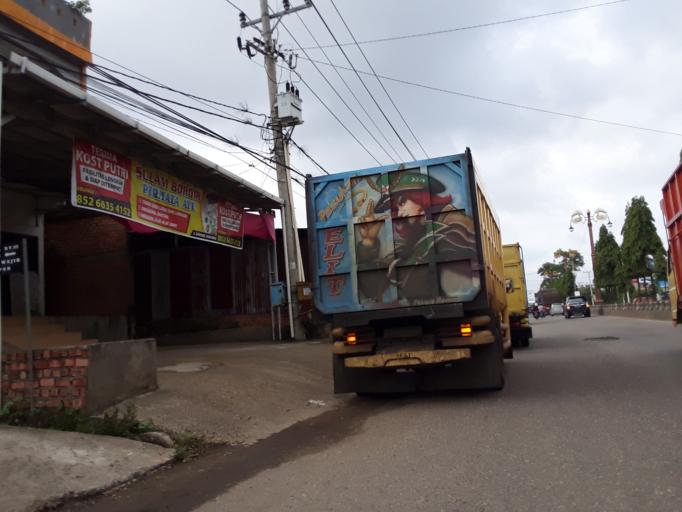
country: ID
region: Jambi
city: Muara Bulian
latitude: -1.7124
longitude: 103.2551
